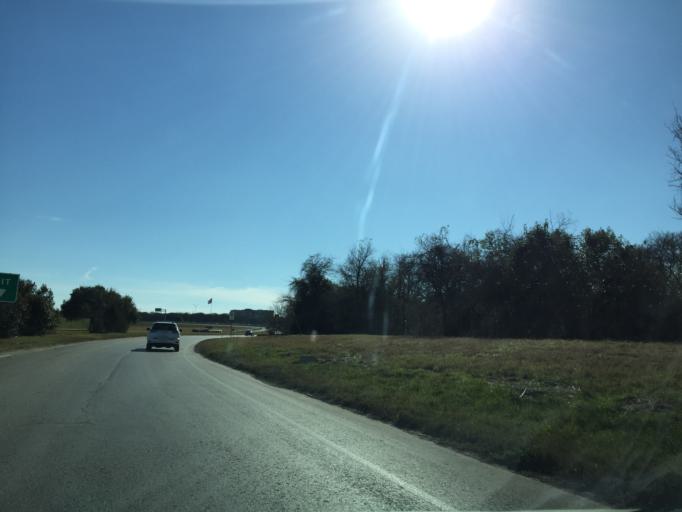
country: US
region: Texas
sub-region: Travis County
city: Austin
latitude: 30.2253
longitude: -97.6833
